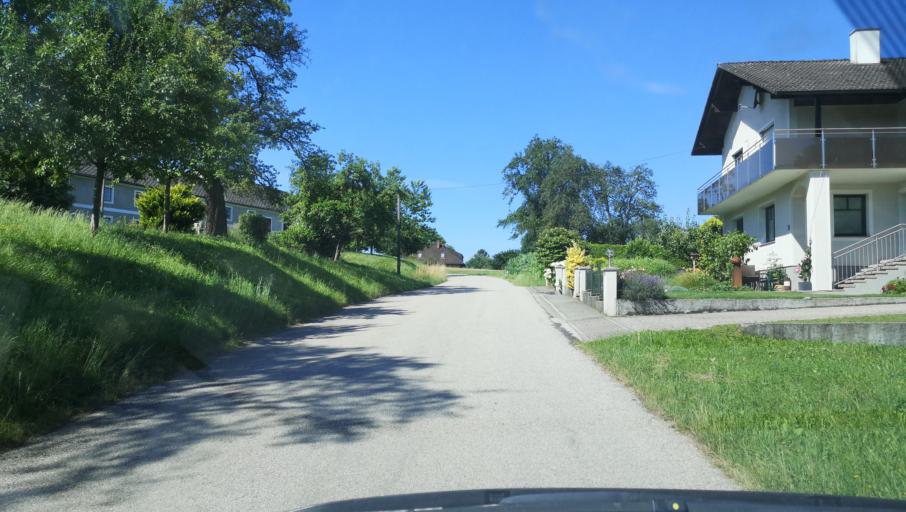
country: AT
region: Lower Austria
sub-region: Politischer Bezirk Amstetten
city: Euratsfeld
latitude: 48.0672
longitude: 14.9250
